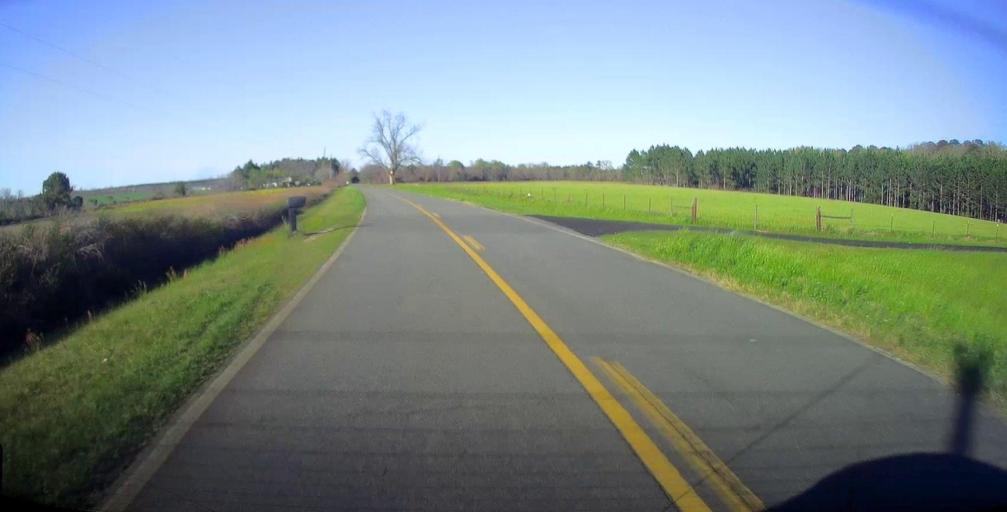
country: US
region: Georgia
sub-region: Pulaski County
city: Hawkinsville
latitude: 32.3160
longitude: -83.5727
